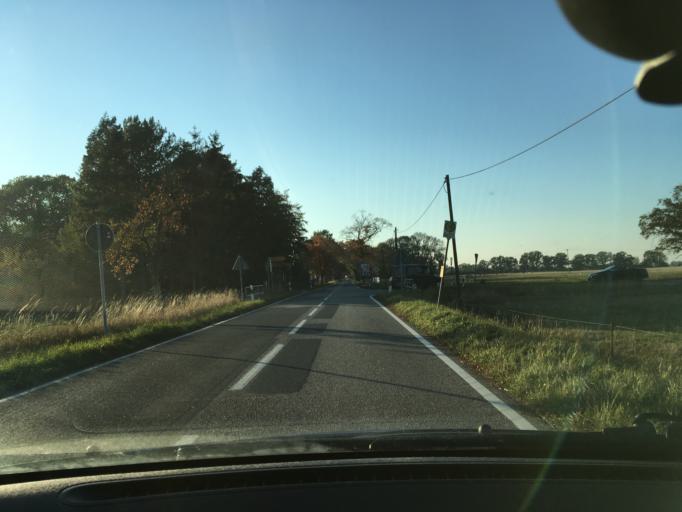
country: DE
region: Lower Saxony
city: Bleckede
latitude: 53.3037
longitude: 10.7875
